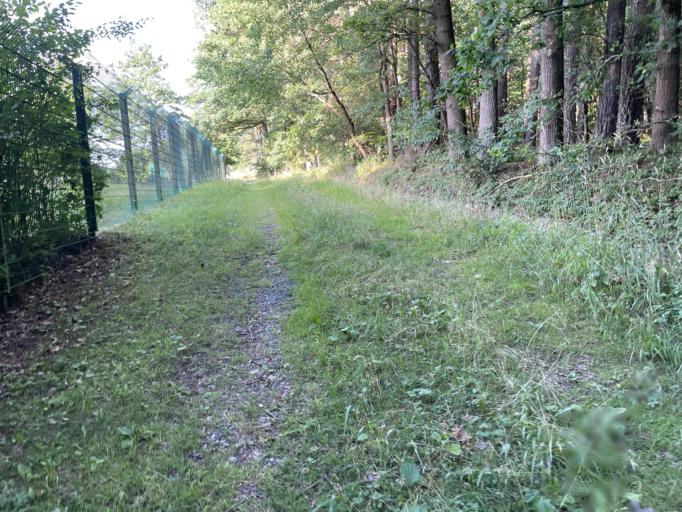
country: DE
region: Bavaria
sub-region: Upper Franconia
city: Neunkirchen am Main
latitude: 49.9482
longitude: 11.6440
